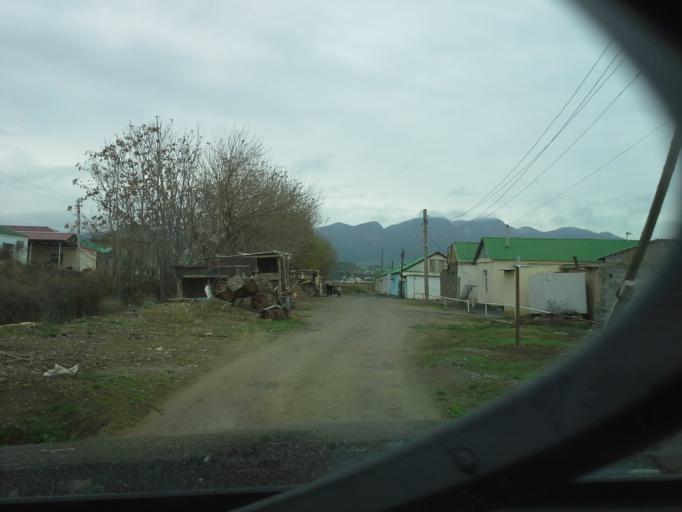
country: TM
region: Ahal
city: Abadan
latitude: 37.9624
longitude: 58.2307
